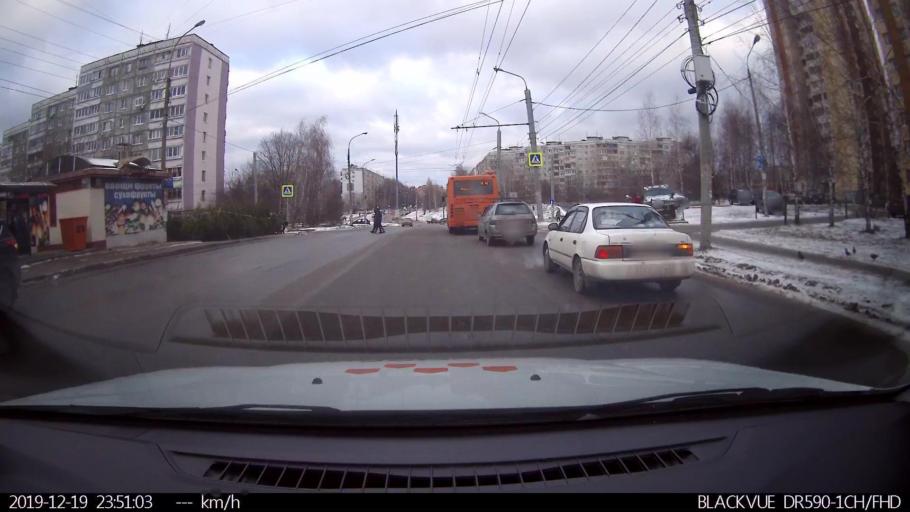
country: RU
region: Vologda
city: Lipin Bor
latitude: 60.9938
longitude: 37.9604
